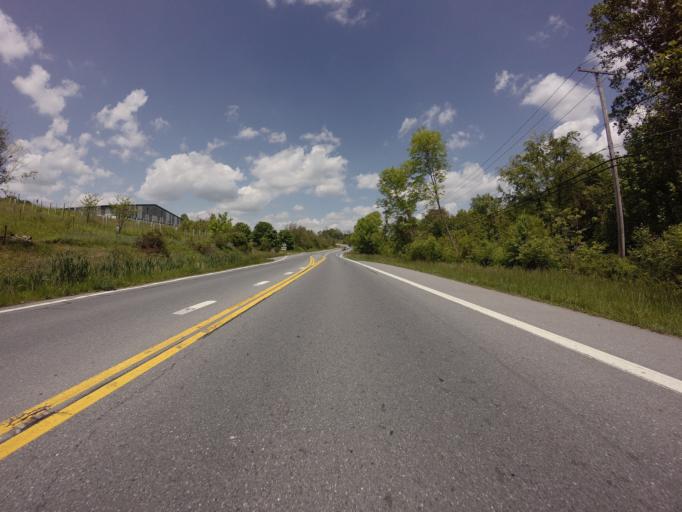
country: US
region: Maryland
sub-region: Frederick County
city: Green Valley
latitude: 39.3209
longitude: -77.2841
